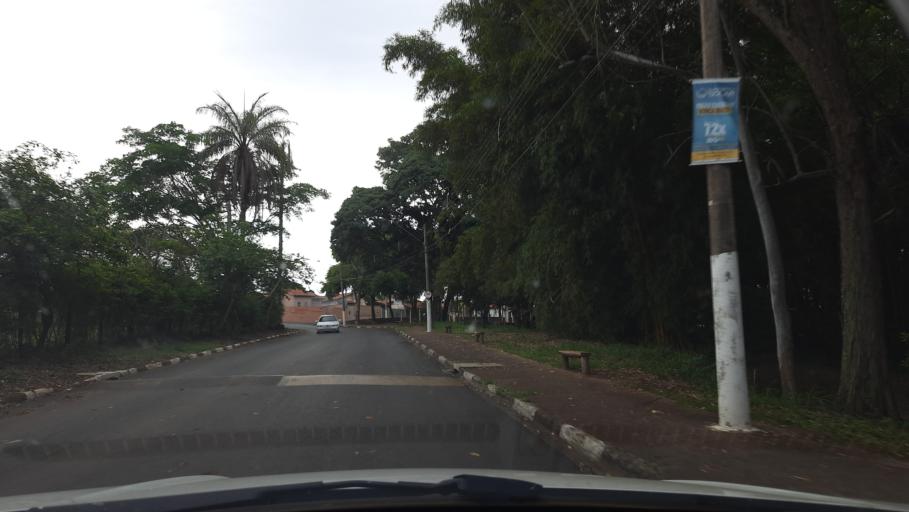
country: BR
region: Sao Paulo
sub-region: Casa Branca
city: Casa Branca
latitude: -21.7823
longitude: -47.0882
